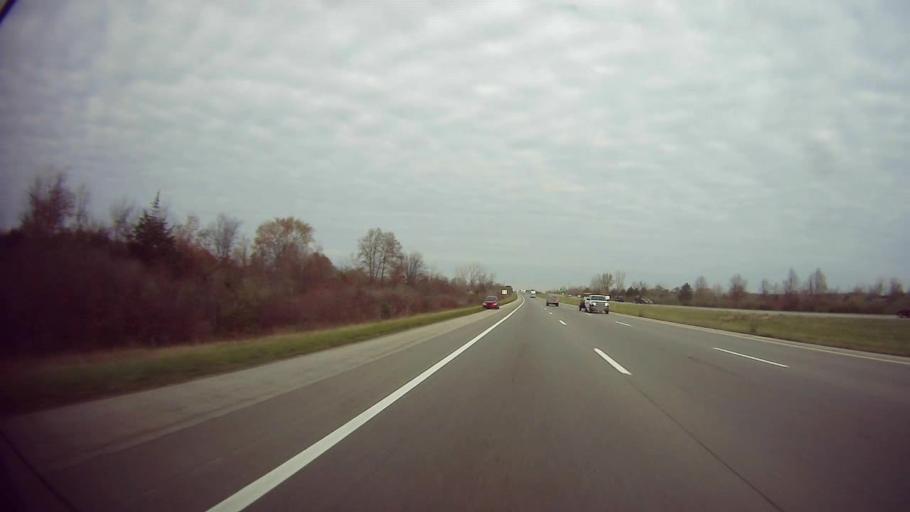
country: US
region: Michigan
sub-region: Monroe County
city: Carleton
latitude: 42.0748
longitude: -83.3690
